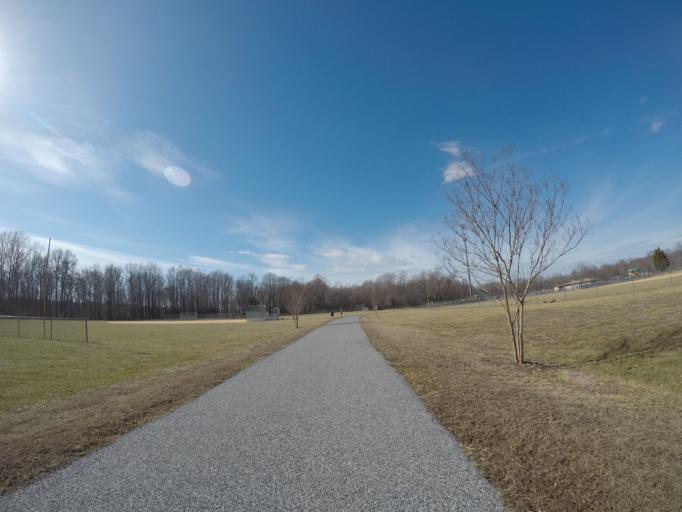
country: US
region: Maryland
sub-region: Charles County
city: Bennsville
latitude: 38.5983
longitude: -77.0176
